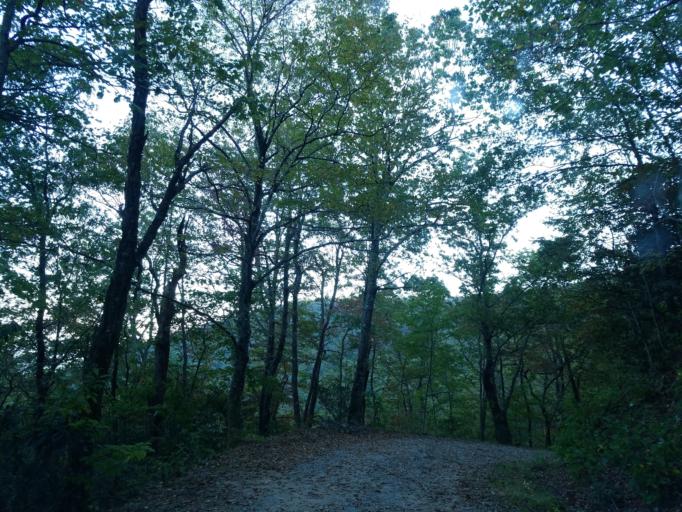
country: US
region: Georgia
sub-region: Dawson County
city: Dawsonville
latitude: 34.5997
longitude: -84.2110
